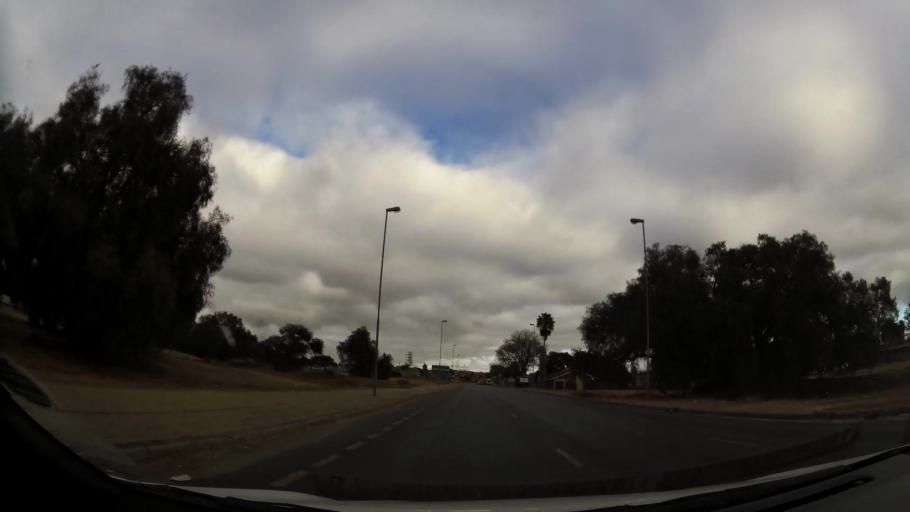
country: ZA
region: Limpopo
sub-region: Capricorn District Municipality
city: Polokwane
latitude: -23.9205
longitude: 29.4540
